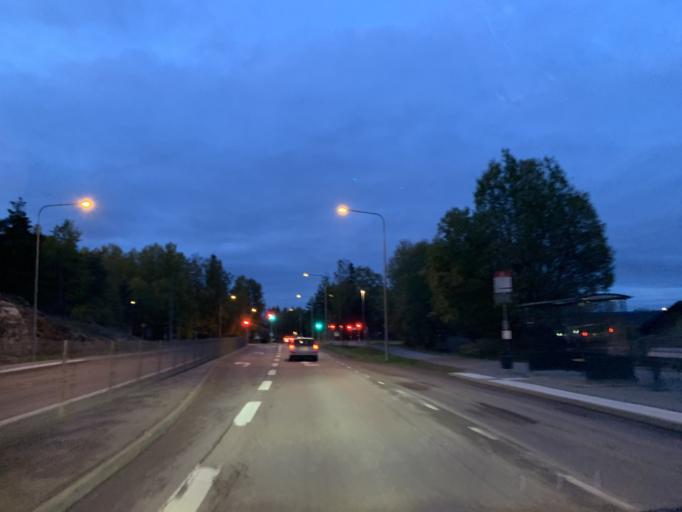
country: SE
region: Stockholm
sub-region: Botkyrka Kommun
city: Tumba
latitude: 59.1822
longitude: 17.8150
